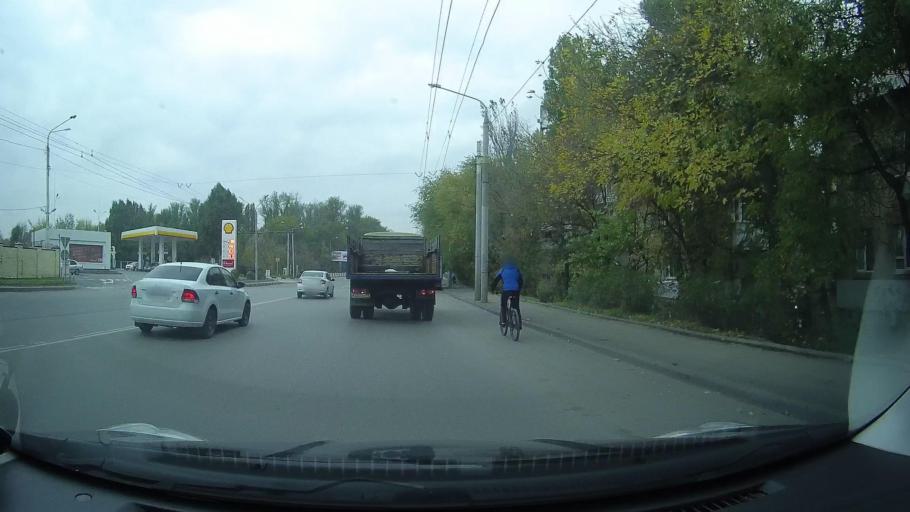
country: RU
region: Rostov
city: Severnyy
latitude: 47.2608
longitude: 39.6878
